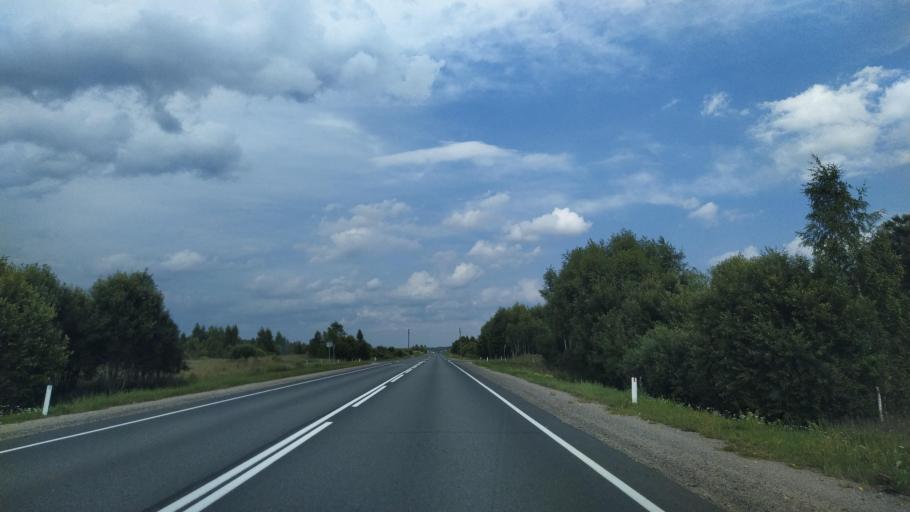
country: RU
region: Pskov
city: Porkhov
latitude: 57.9619
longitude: 29.6718
